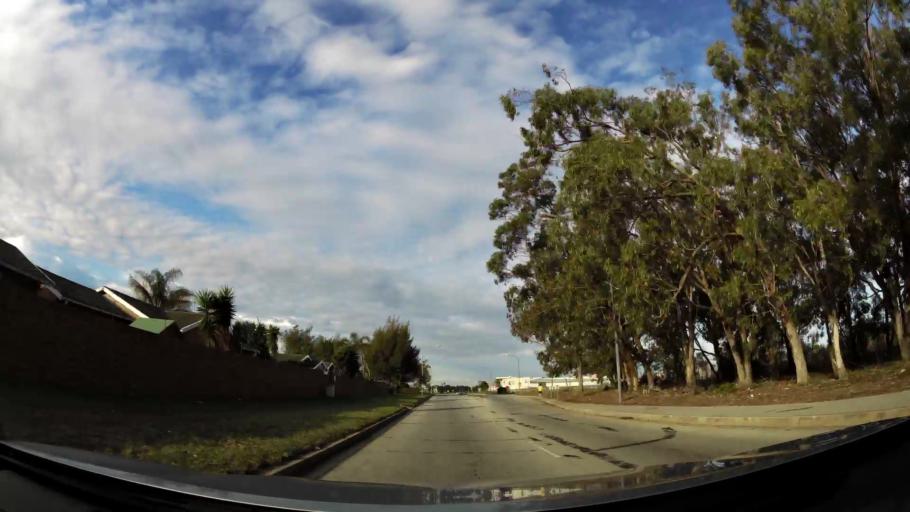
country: ZA
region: Eastern Cape
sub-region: Nelson Mandela Bay Metropolitan Municipality
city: Port Elizabeth
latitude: -33.9576
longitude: 25.4994
